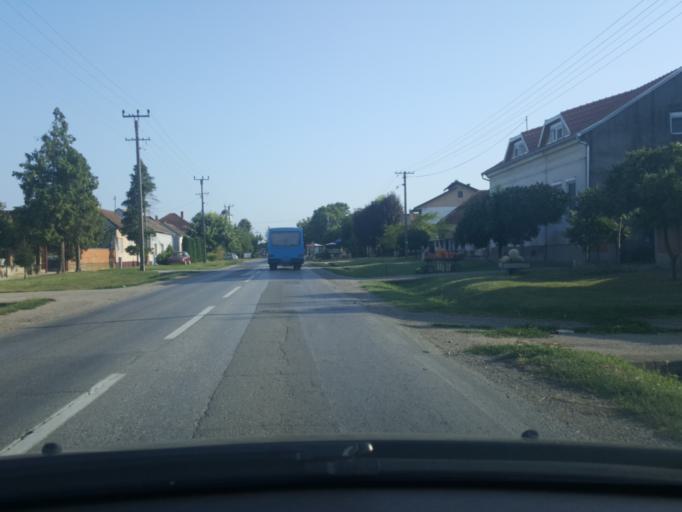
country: RS
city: Hrtkovci
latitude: 44.8838
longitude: 19.7633
